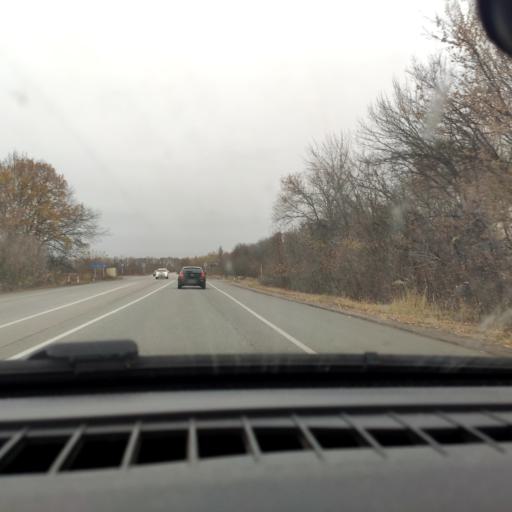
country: RU
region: Voronezj
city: Devitsa
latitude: 51.6001
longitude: 38.9726
